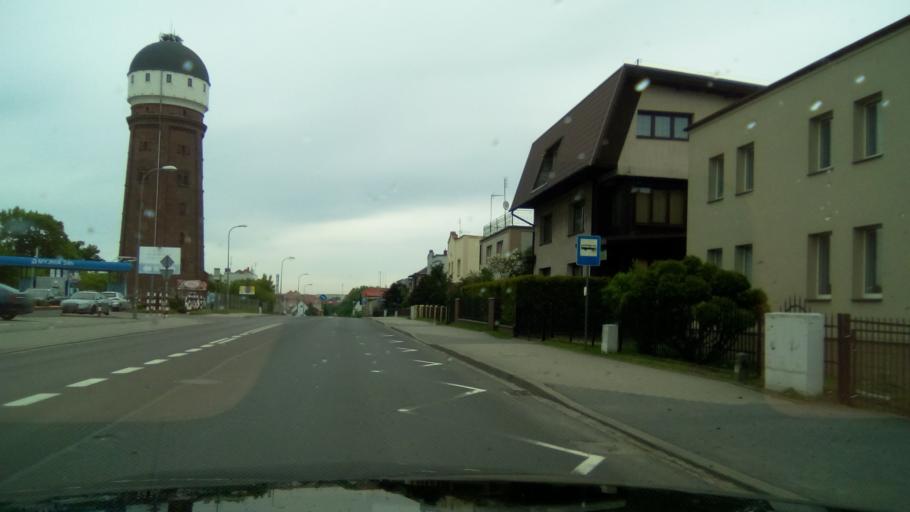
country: PL
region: Pomeranian Voivodeship
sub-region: Powiat chojnicki
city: Chojnice
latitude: 53.6904
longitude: 17.5523
